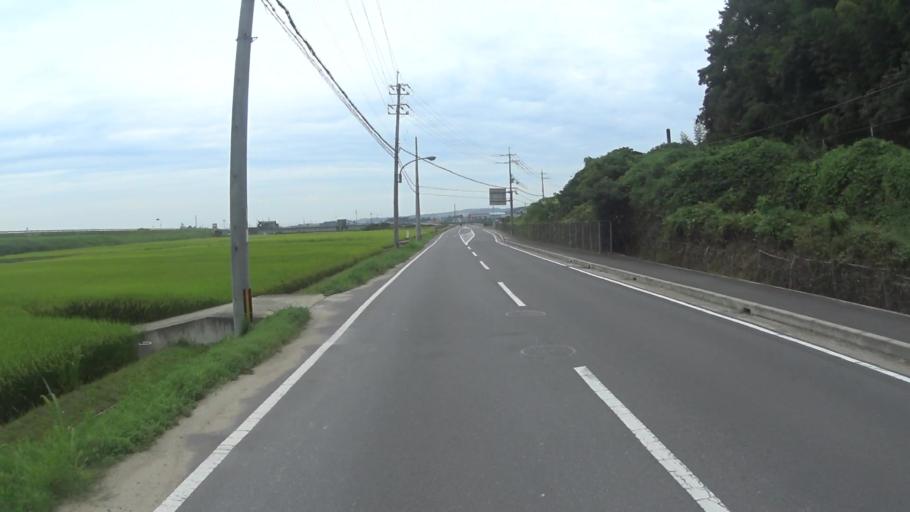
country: JP
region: Kyoto
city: Tanabe
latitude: 34.8079
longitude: 135.8067
